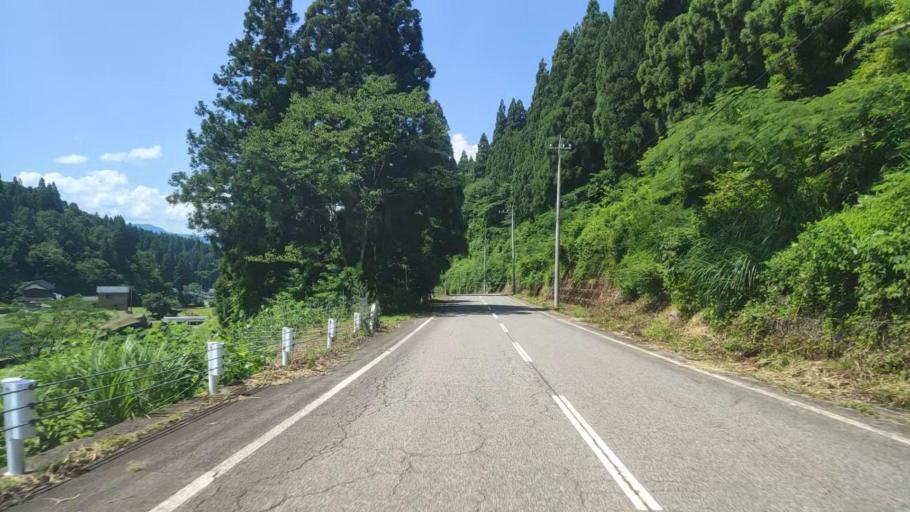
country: JP
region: Fukui
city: Katsuyama
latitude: 36.1098
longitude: 136.4991
